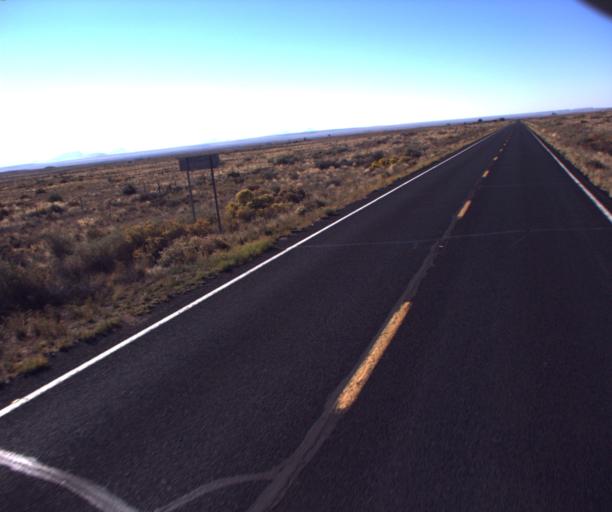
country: US
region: Arizona
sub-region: Navajo County
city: First Mesa
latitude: 35.7846
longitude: -110.5000
